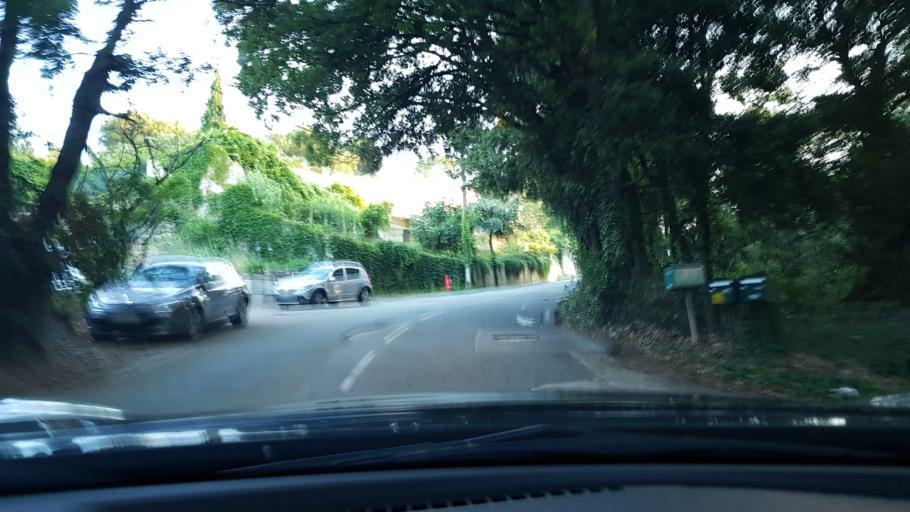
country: FR
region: Provence-Alpes-Cote d'Azur
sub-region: Departement des Alpes-Maritimes
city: Vallauris
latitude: 43.5859
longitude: 7.0462
